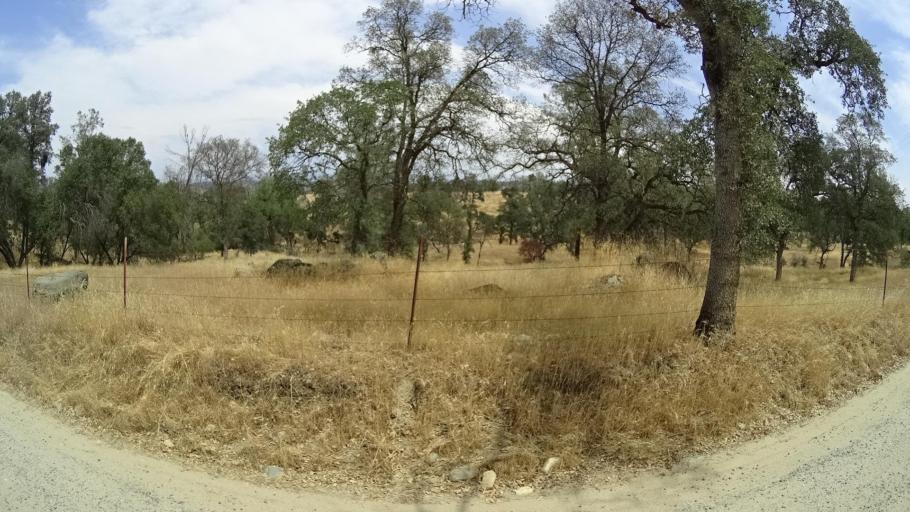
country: US
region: California
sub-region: Madera County
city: Ahwahnee
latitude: 37.3679
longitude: -119.8697
